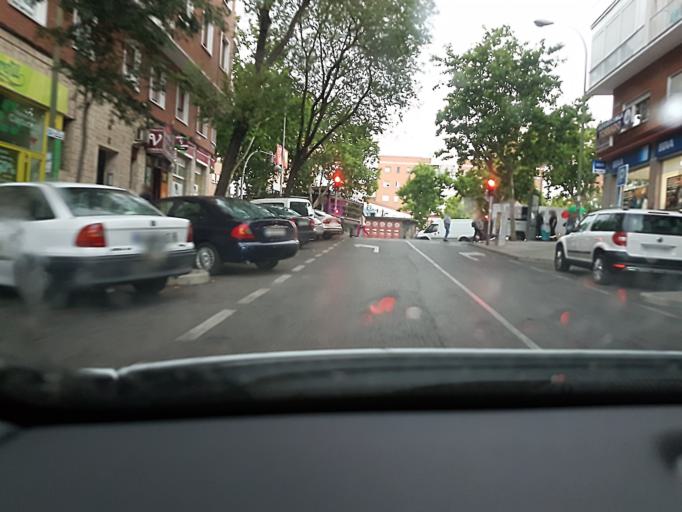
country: ES
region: Madrid
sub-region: Provincia de Madrid
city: Moratalaz
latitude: 40.4328
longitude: -3.6479
